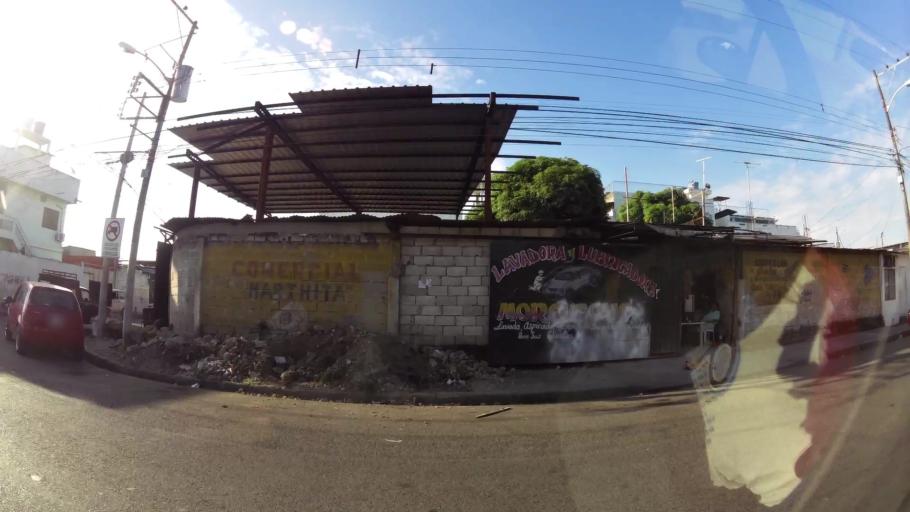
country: EC
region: Guayas
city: Guayaquil
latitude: -2.2269
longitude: -79.9070
